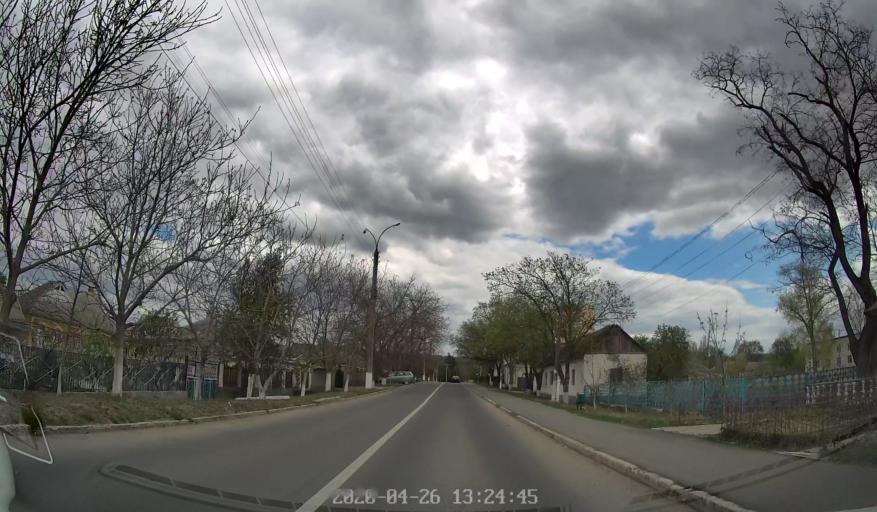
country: MD
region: Criuleni
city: Criuleni
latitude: 47.2068
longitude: 29.1640
